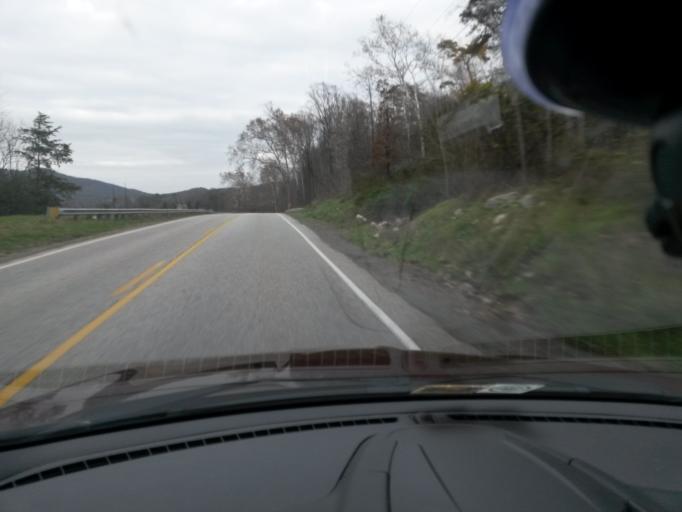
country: US
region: Virginia
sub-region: Rockbridge County
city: Glasgow
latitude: 37.6365
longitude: -79.4355
